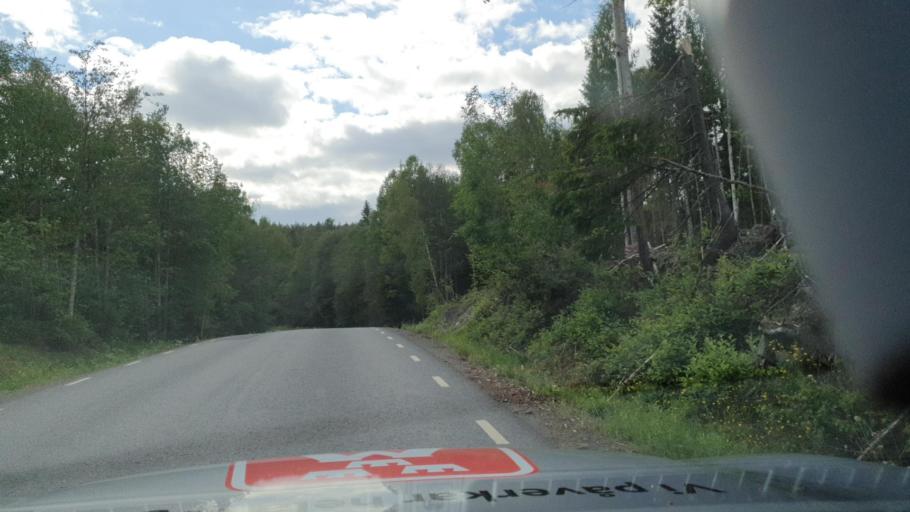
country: SE
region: Vaesternorrland
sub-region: Haernoesands Kommun
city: Haernoesand
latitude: 62.8083
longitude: 18.0290
